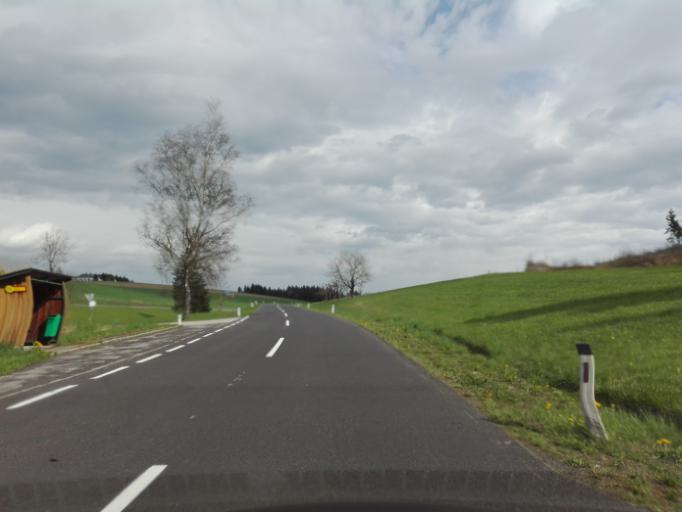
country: AT
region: Upper Austria
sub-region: Politischer Bezirk Rohrbach
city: Kleinzell im Muehlkreis
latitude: 48.4707
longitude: 14.0157
